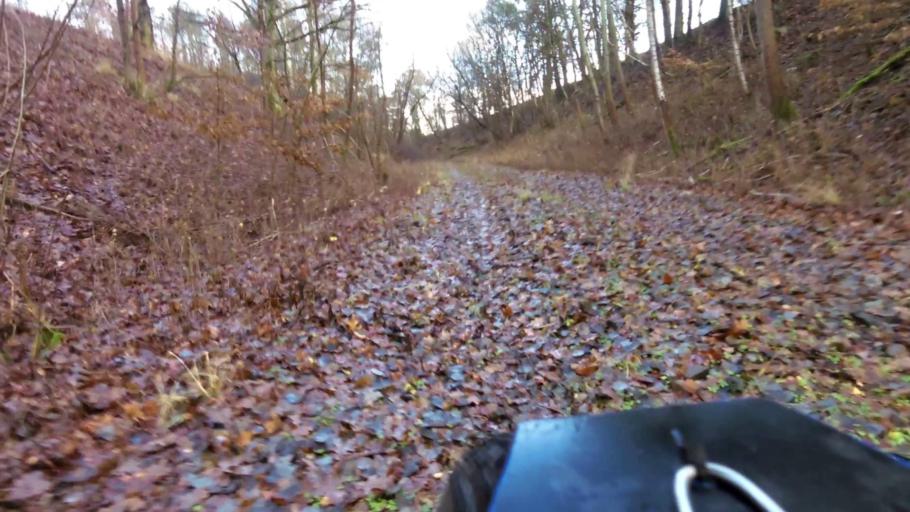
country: PL
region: Lubusz
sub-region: Powiat gorzowski
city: Jenin
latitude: 52.7267
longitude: 15.1390
